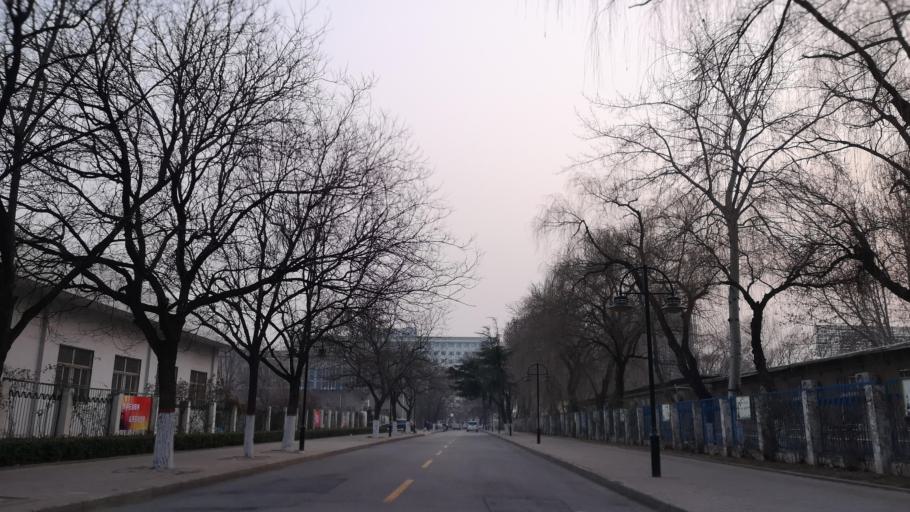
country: CN
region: Henan Sheng
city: Zhongyuanlu
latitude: 35.7799
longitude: 115.0740
